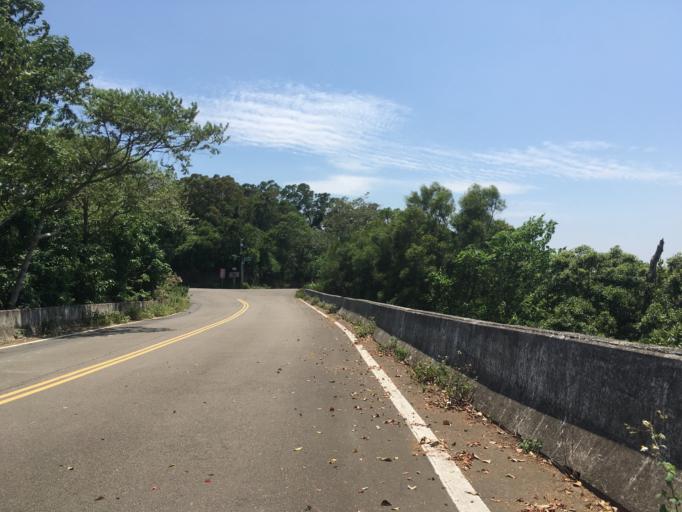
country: TW
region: Taiwan
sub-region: Hsinchu
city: Hsinchu
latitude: 24.7338
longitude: 120.9873
